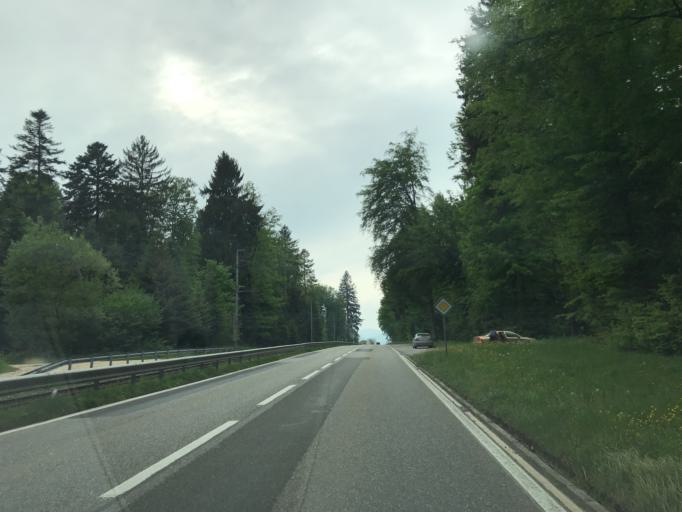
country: CH
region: Solothurn
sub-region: Bezirk Gaeu
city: Oensingen
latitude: 47.2504
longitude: 7.7300
